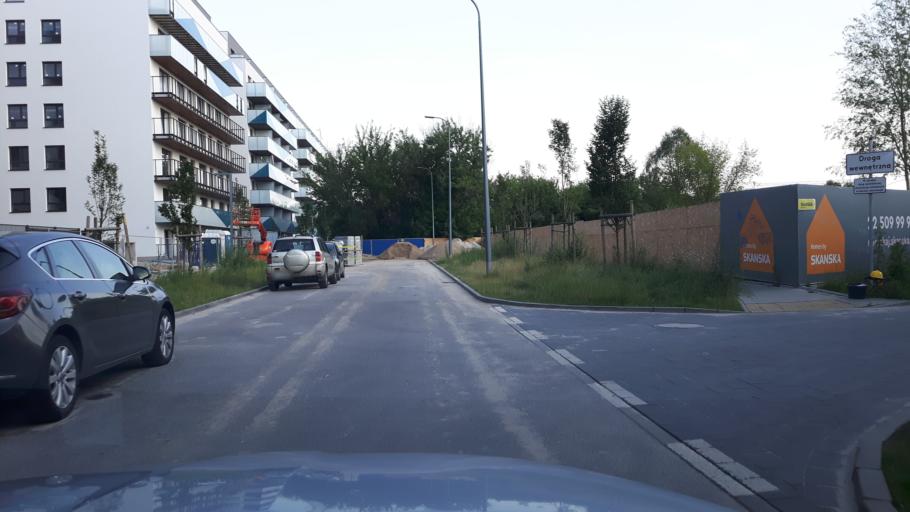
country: PL
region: Masovian Voivodeship
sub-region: Warszawa
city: Mokotow
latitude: 52.1835
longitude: 21.0429
